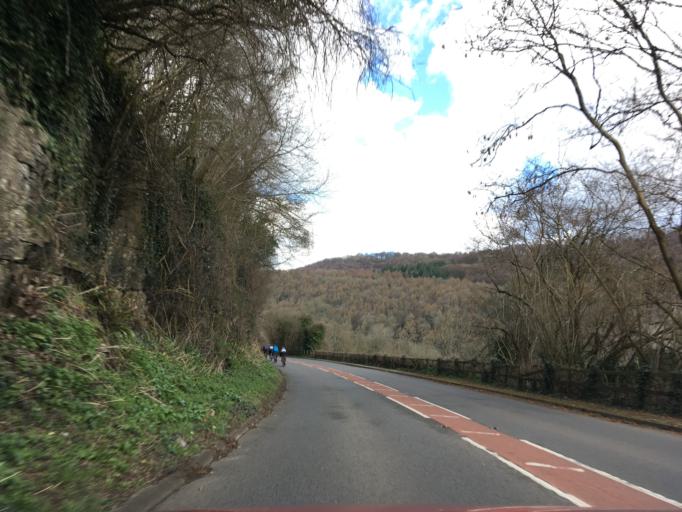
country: GB
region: Wales
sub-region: Monmouthshire
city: Tintern
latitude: 51.6902
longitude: -2.6716
